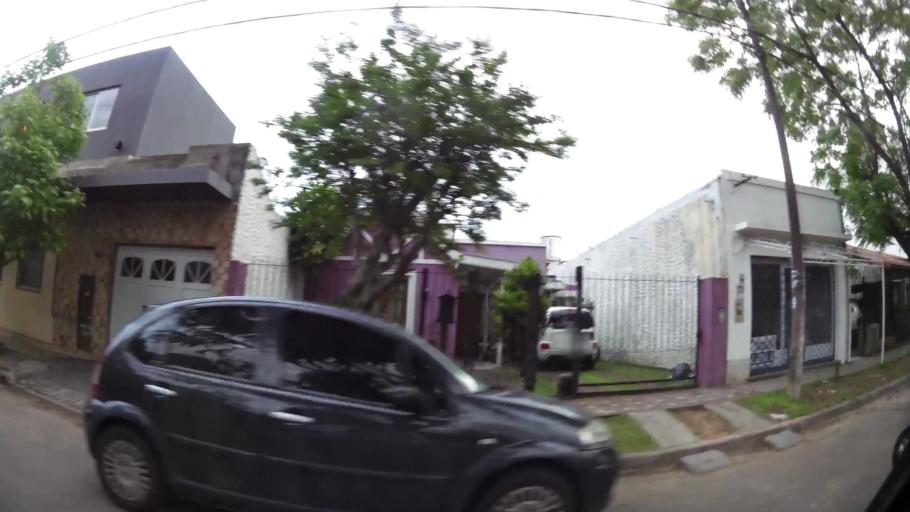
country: AR
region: Buenos Aires
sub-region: Partido de Quilmes
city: Quilmes
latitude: -34.7504
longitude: -58.2350
